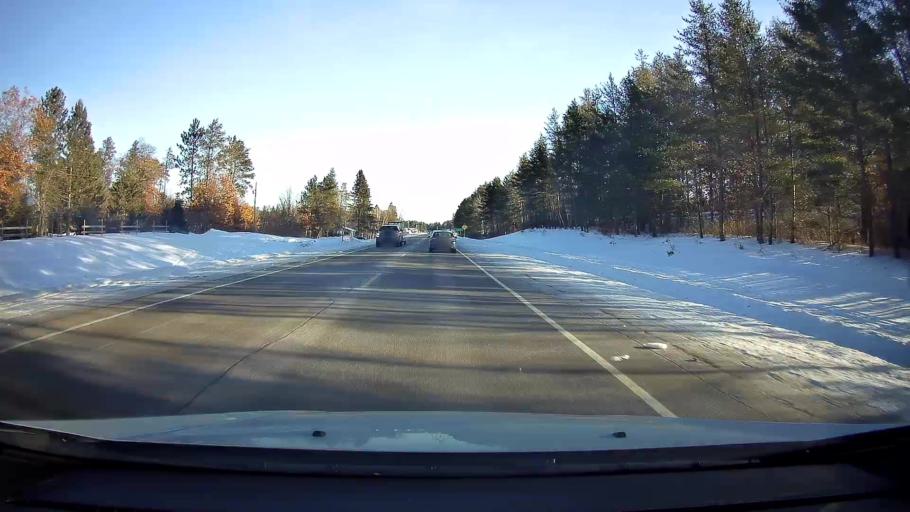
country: US
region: Wisconsin
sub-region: Sawyer County
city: Hayward
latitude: 45.9424
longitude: -91.6958
